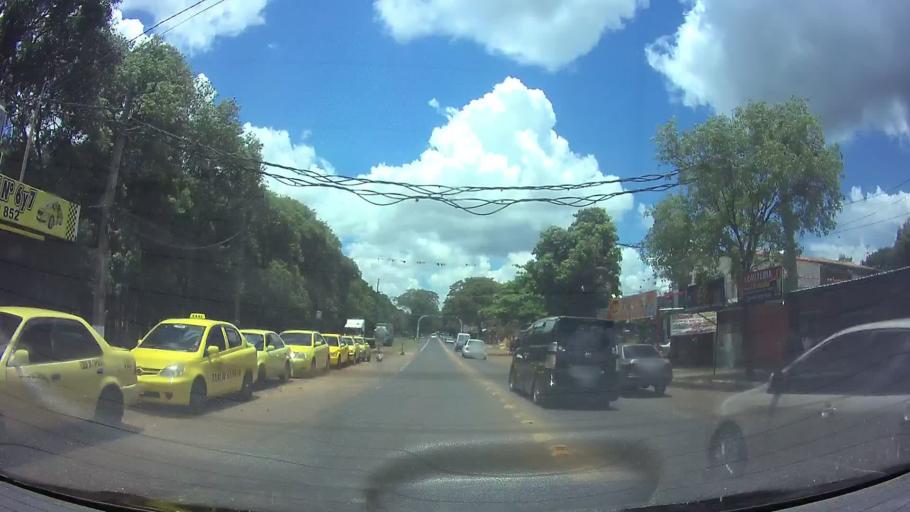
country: PY
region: Central
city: Capiata
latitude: -25.3620
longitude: -57.4281
